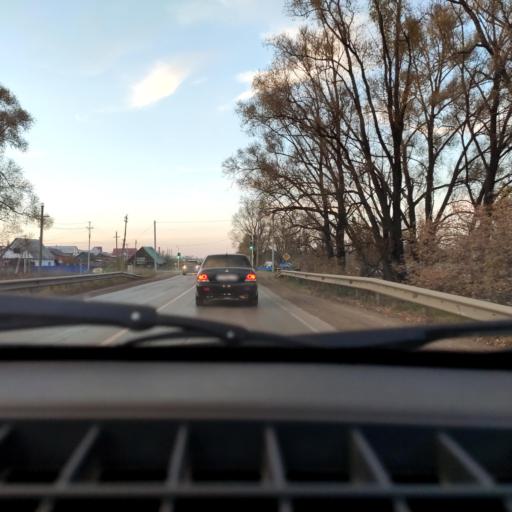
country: RU
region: Bashkortostan
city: Avdon
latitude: 54.7345
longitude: 55.8034
